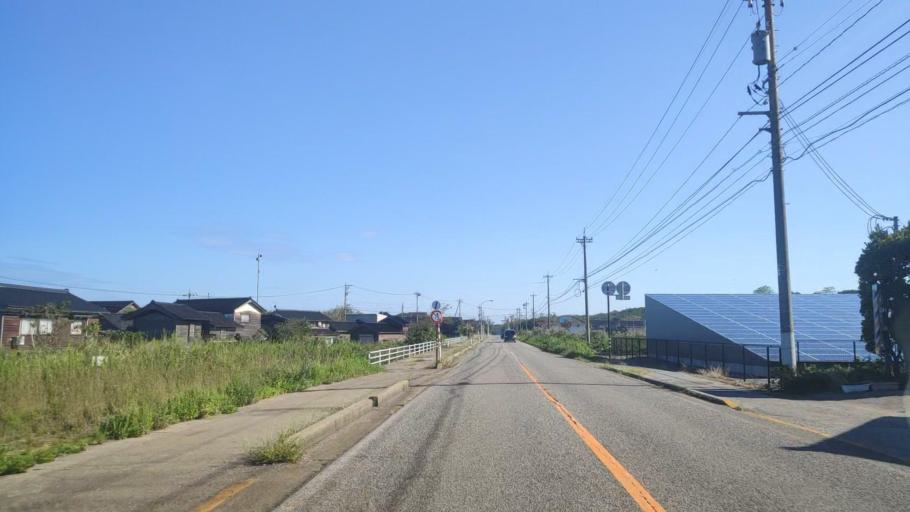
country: JP
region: Ishikawa
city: Hakui
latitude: 36.9515
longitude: 136.7661
